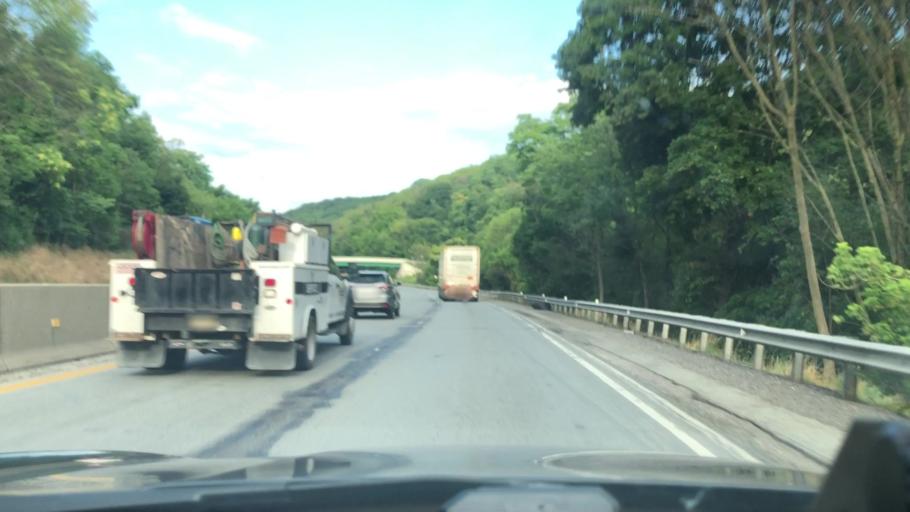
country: US
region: Pennsylvania
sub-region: Berks County
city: Hamburg
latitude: 40.5738
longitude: -75.8765
